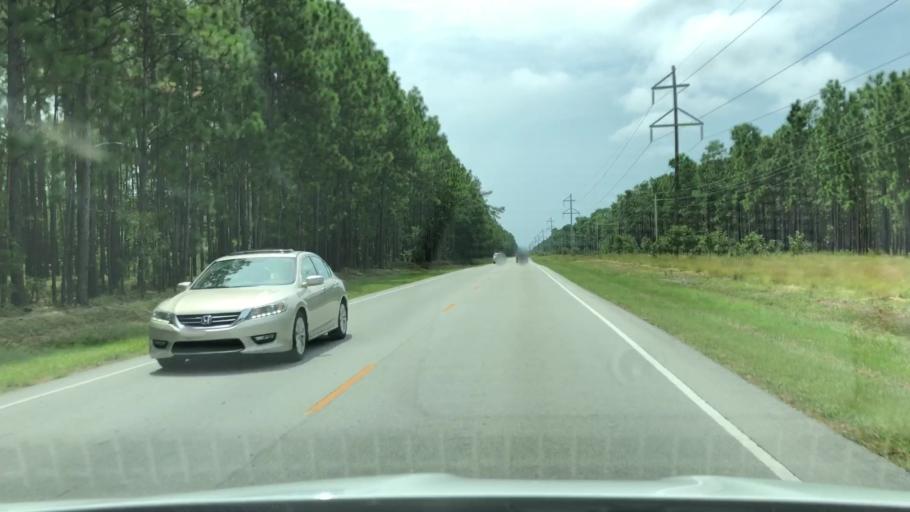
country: US
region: North Carolina
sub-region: Carteret County
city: Newport
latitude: 34.7663
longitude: -76.8678
